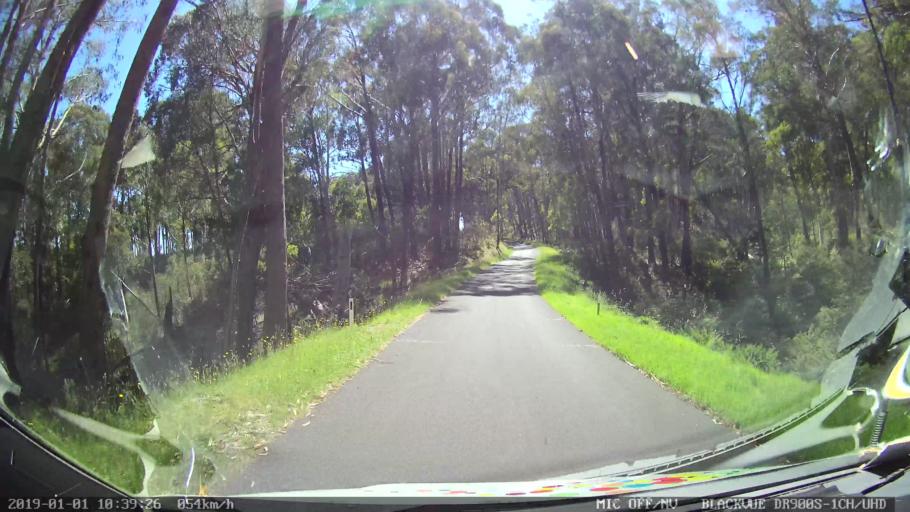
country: AU
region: New South Wales
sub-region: Snowy River
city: Jindabyne
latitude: -36.0403
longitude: 148.3043
